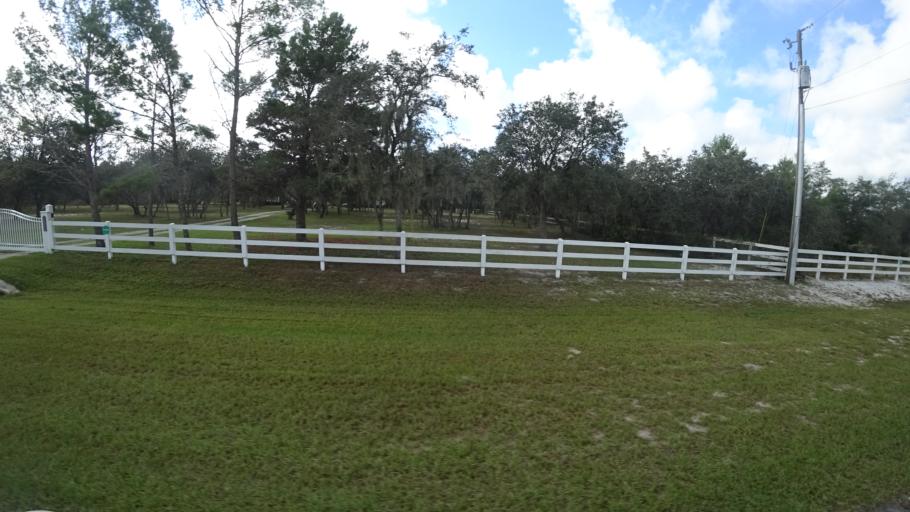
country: US
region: Florida
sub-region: Sarasota County
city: Lake Sarasota
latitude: 27.3591
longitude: -82.2403
